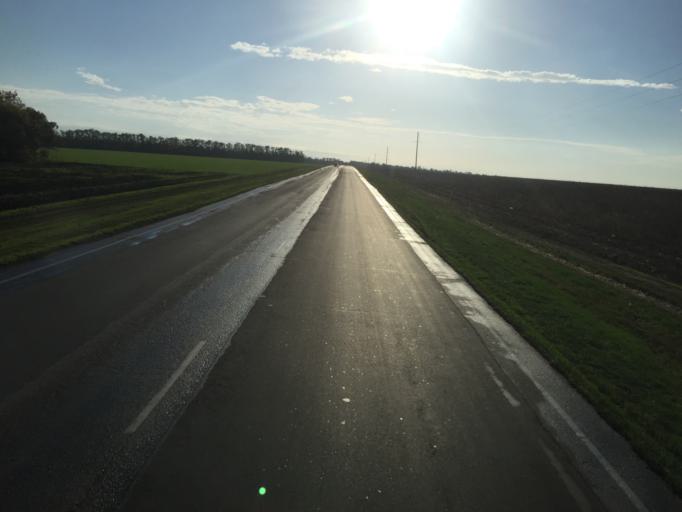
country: RU
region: Rostov
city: Mechetinskaya
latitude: 46.7930
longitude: 40.3882
